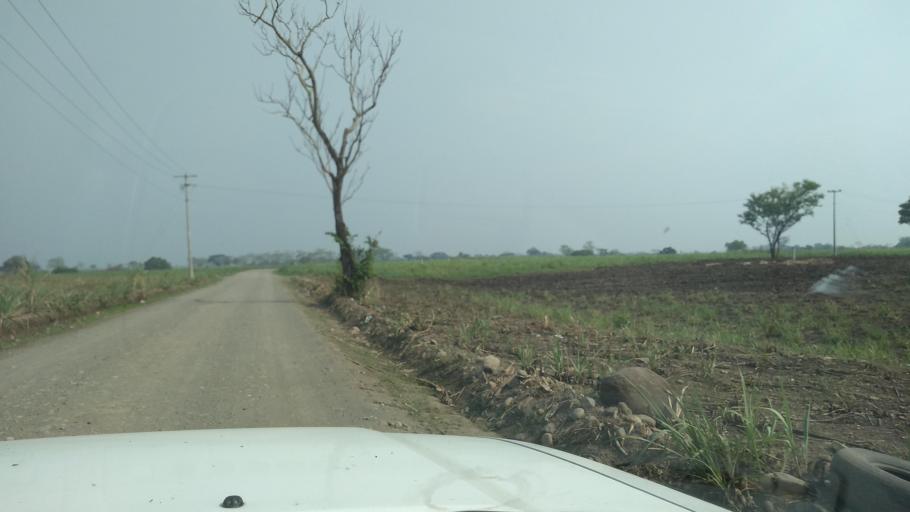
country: MX
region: Veracruz
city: Tezonapa
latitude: 18.6252
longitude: -96.6084
